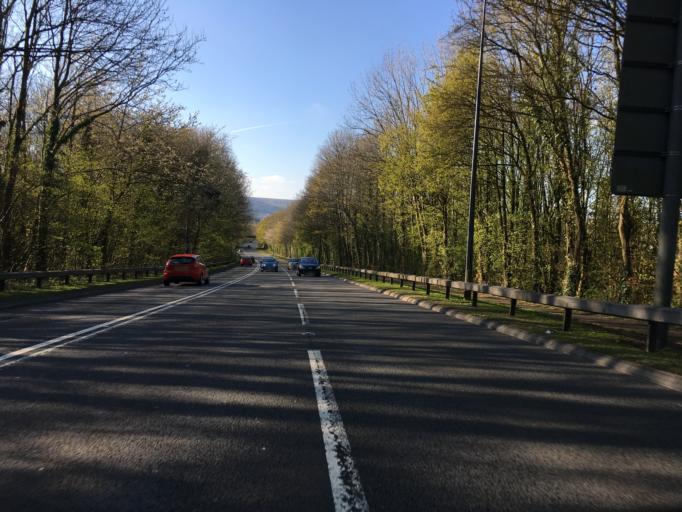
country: GB
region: Wales
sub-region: Torfaen County Borough
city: Cwmbran
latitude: 51.6229
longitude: -3.0117
